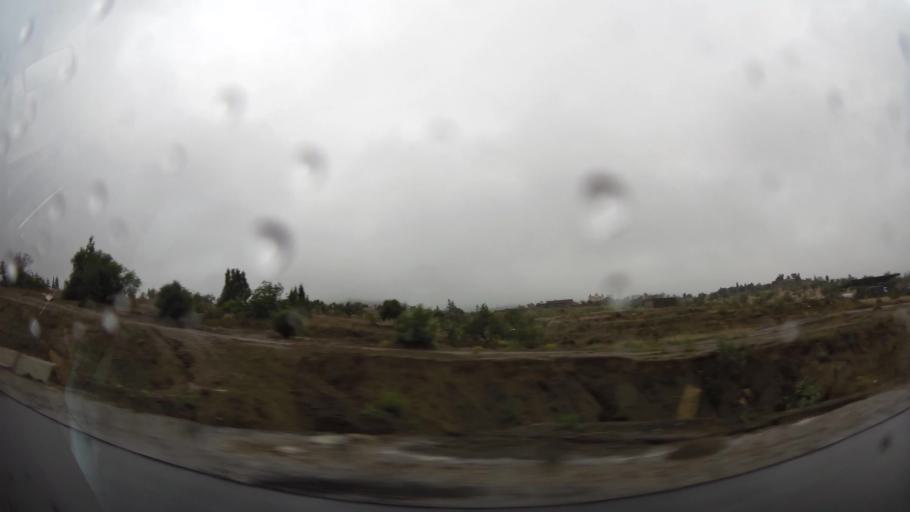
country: MA
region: Oriental
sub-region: Nador
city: Midar
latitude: 34.8618
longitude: -3.7232
